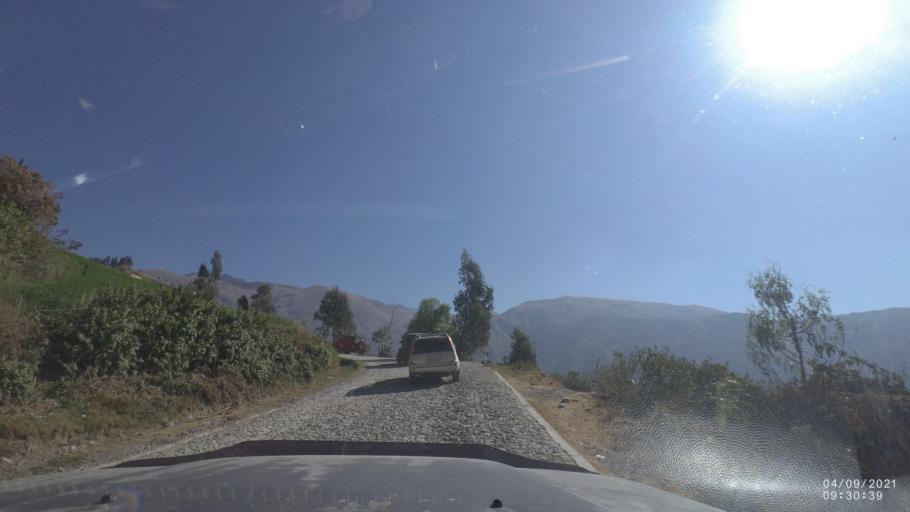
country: BO
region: Cochabamba
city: Sipe Sipe
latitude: -17.3529
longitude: -66.3766
